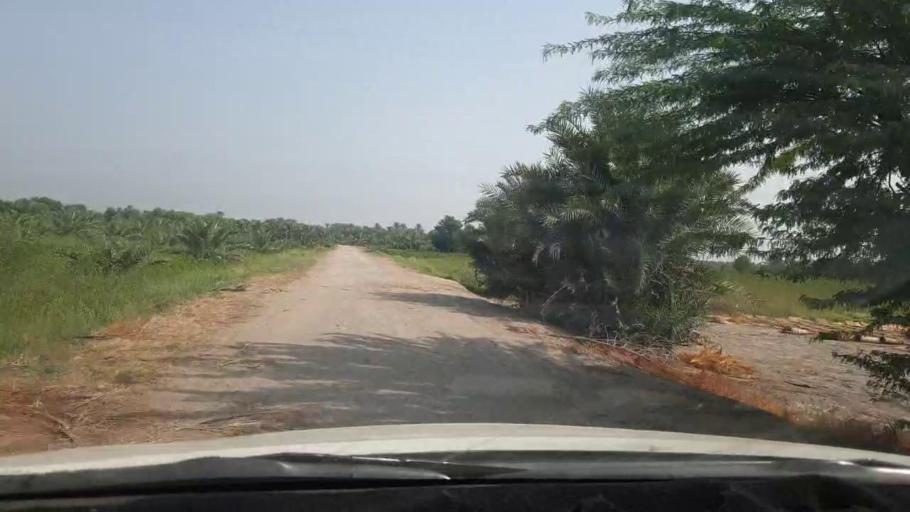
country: PK
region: Sindh
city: Rohri
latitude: 27.6129
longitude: 68.8978
